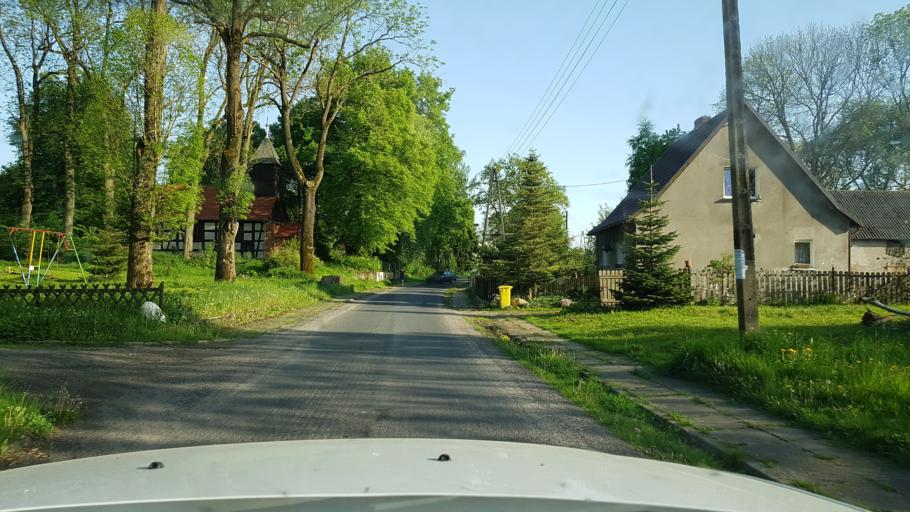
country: PL
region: West Pomeranian Voivodeship
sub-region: Powiat lobeski
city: Radowo Male
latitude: 53.6796
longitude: 15.3499
